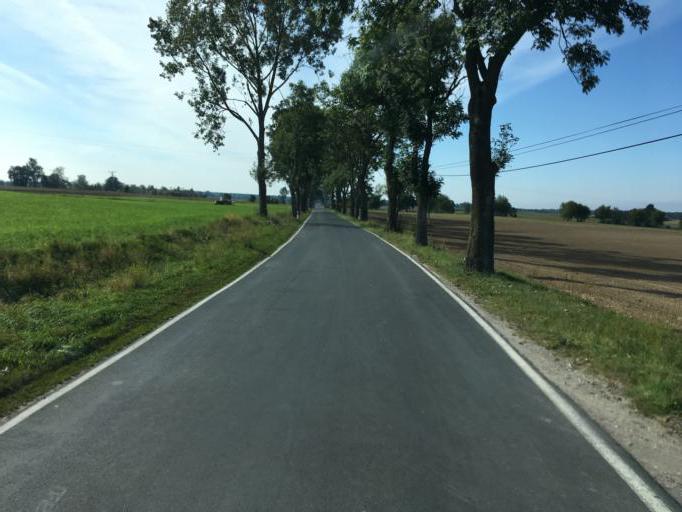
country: PL
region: Kujawsko-Pomorskie
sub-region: Powiat swiecki
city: Lniano
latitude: 53.5165
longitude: 18.1838
